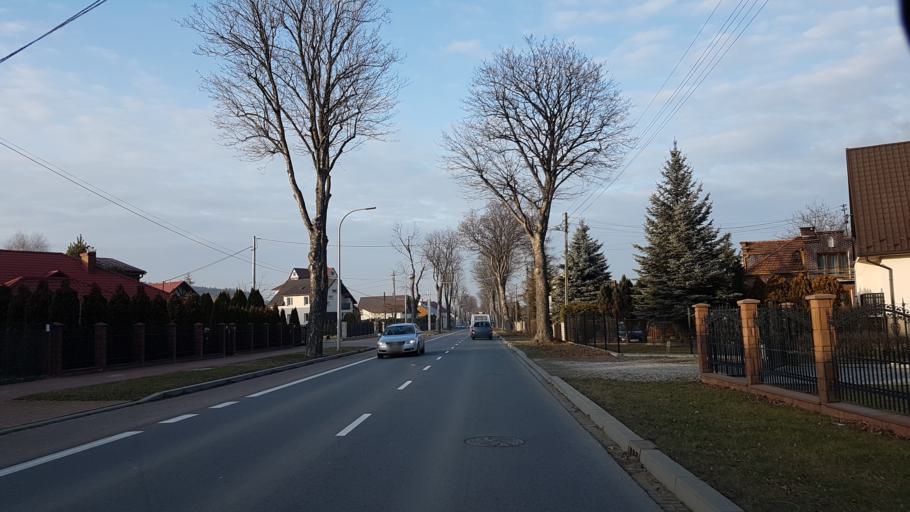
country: PL
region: Lesser Poland Voivodeship
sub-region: Powiat nowosadecki
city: Stary Sacz
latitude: 49.5477
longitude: 20.6420
